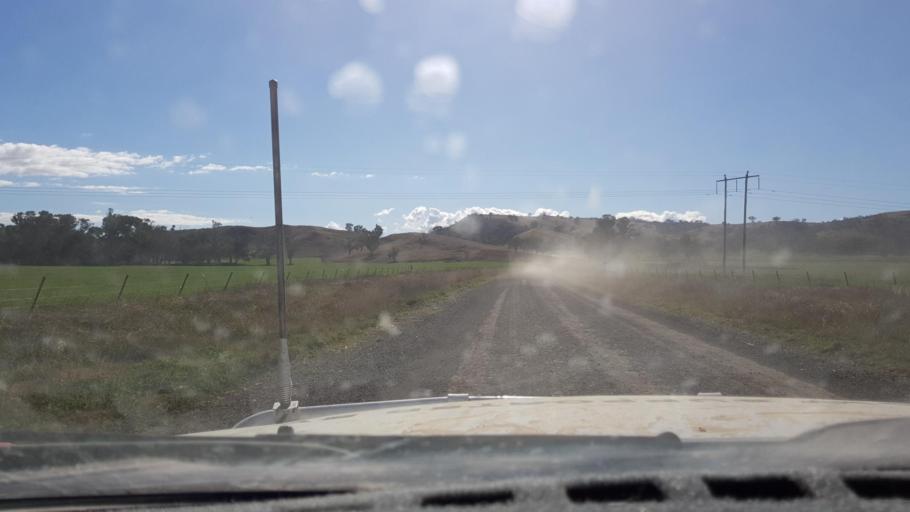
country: AU
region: New South Wales
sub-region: Narrabri
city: Blair Athol
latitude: -30.4458
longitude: 150.4520
